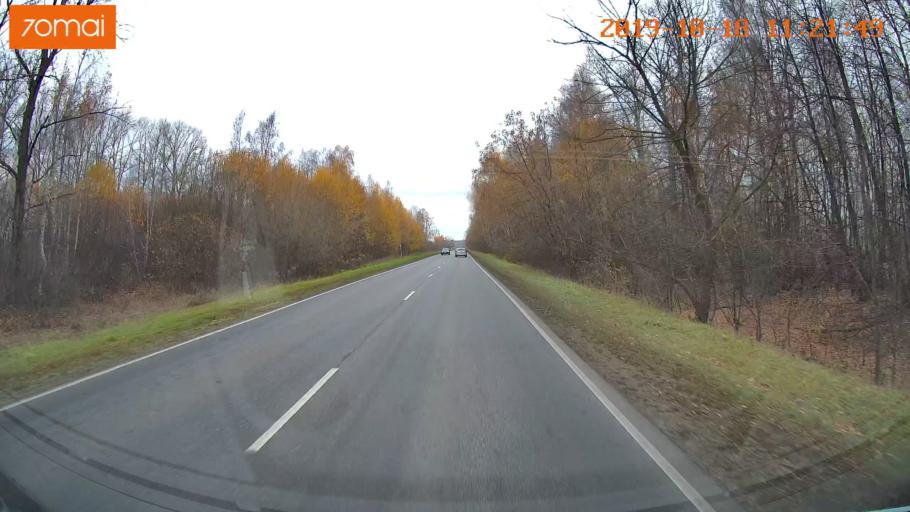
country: RU
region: Tula
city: Kimovsk
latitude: 54.0790
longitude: 38.5709
